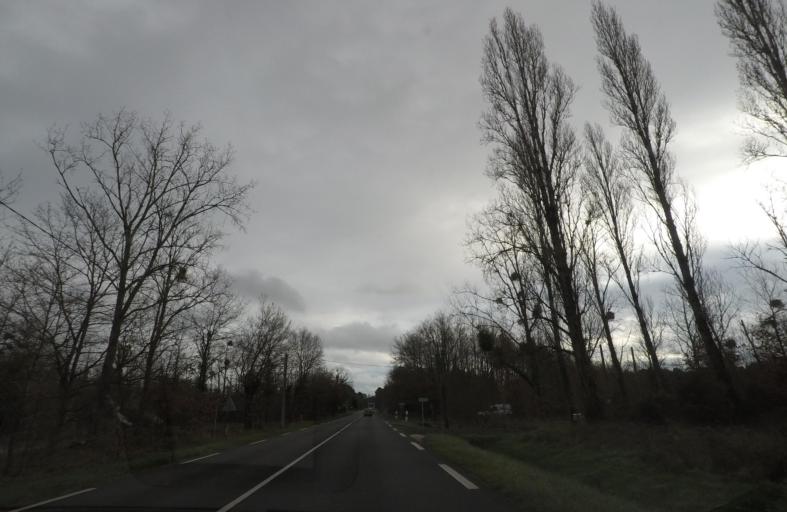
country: FR
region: Centre
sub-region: Departement du Loir-et-Cher
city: Mur-de-Sologne
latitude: 47.4066
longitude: 1.6186
